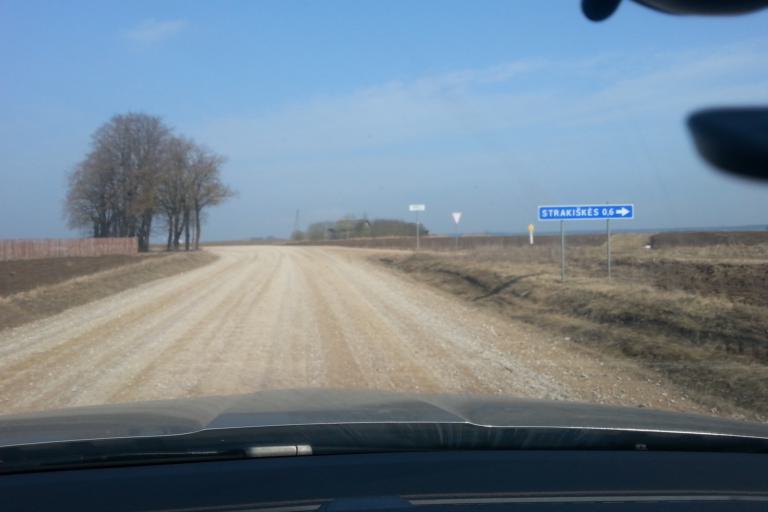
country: LT
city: Trakai
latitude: 54.5848
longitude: 24.9772
